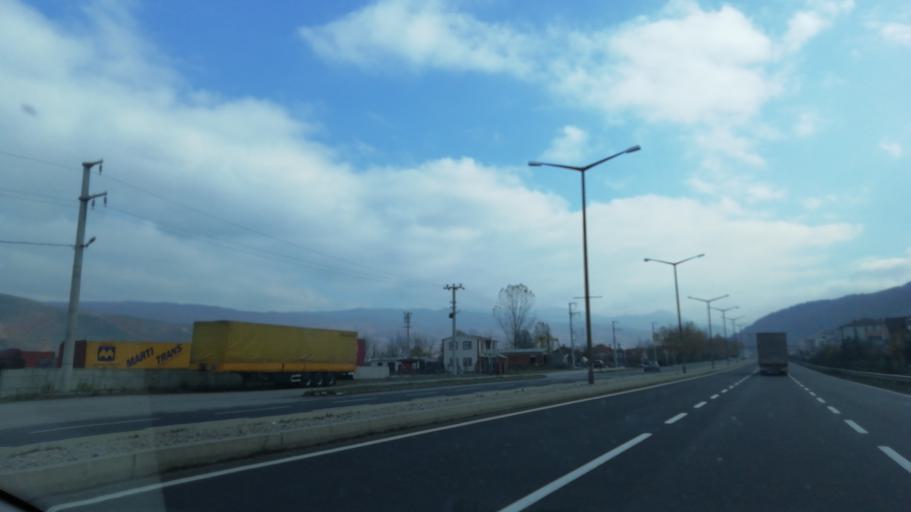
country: TR
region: Duzce
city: Kaynasli
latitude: 40.7752
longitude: 31.3089
